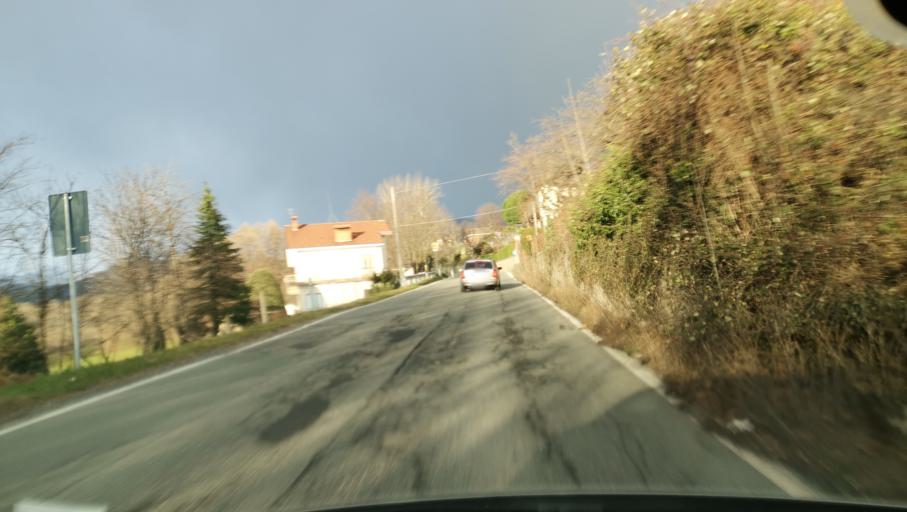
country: IT
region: Piedmont
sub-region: Provincia di Torino
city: Giaveno
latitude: 45.0503
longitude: 7.3299
